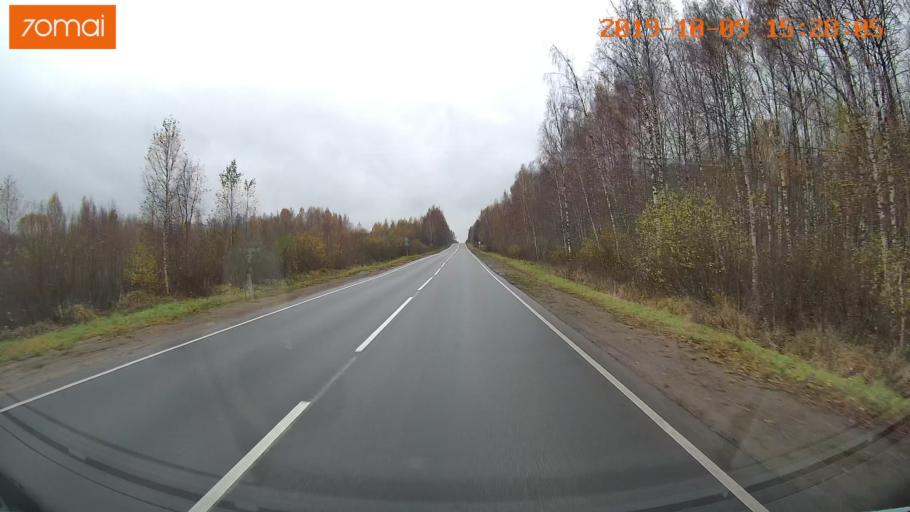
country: RU
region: Kostroma
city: Susanino
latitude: 58.0072
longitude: 41.3660
